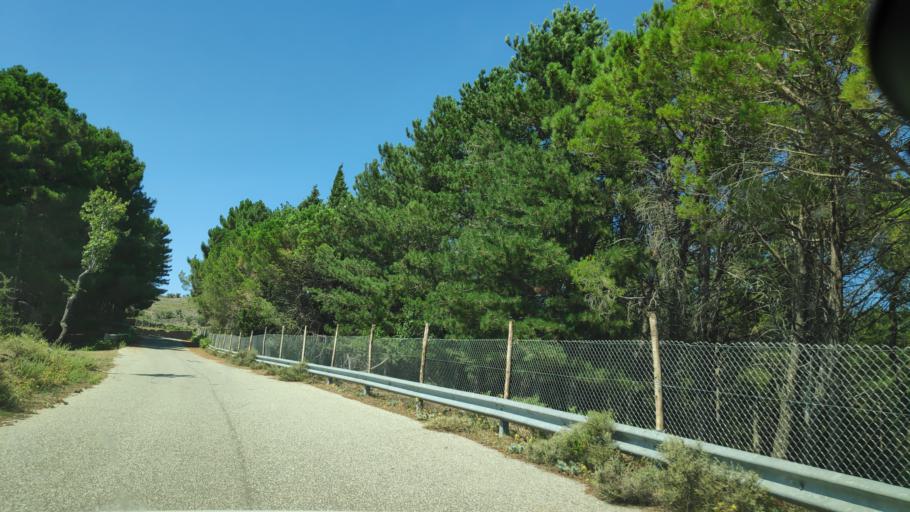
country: IT
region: Calabria
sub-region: Provincia di Reggio Calabria
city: Bova
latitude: 38.0150
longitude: 15.9349
